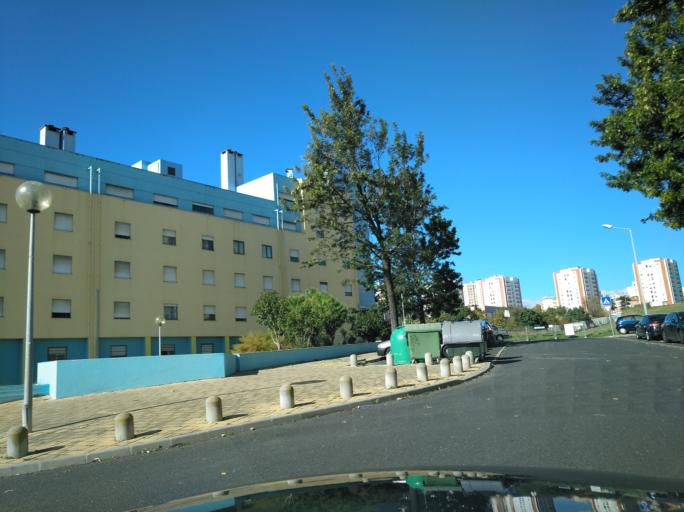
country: PT
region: Lisbon
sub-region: Lisbon
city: Lisbon
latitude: 38.7396
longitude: -9.1096
